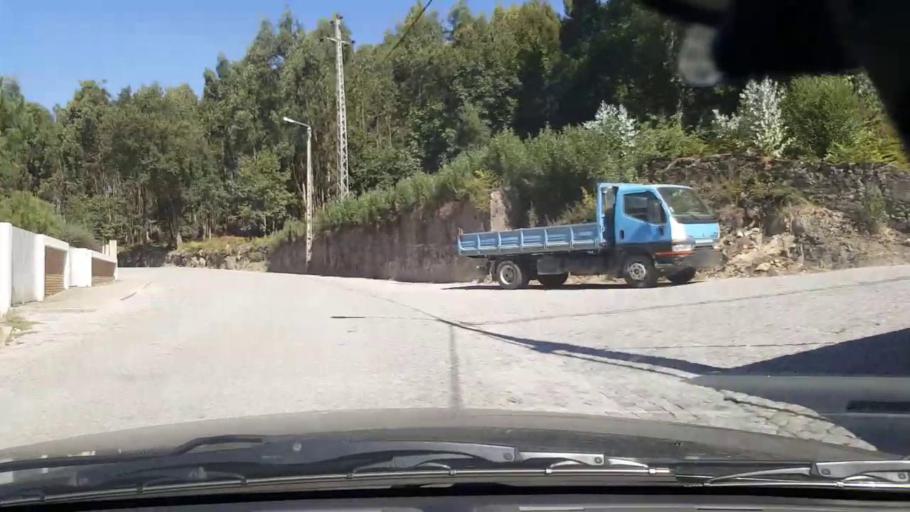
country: PT
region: Porto
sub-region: Maia
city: Gemunde
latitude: 41.3233
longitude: -8.6410
